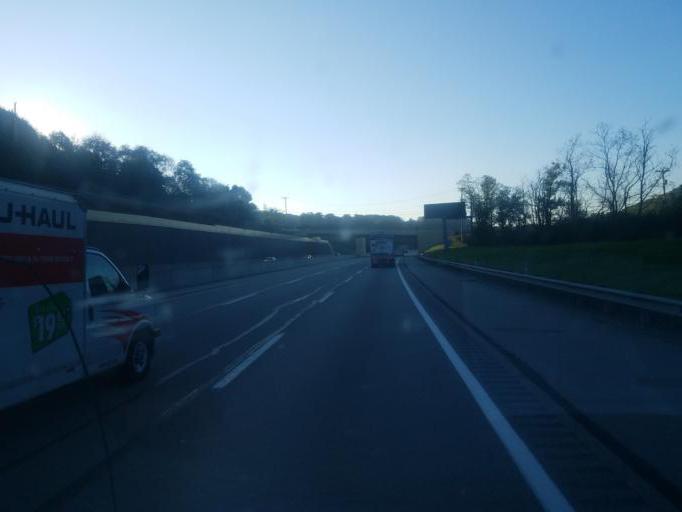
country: US
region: Pennsylvania
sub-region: Allegheny County
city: Gibsonia
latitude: 40.6315
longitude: -79.9867
